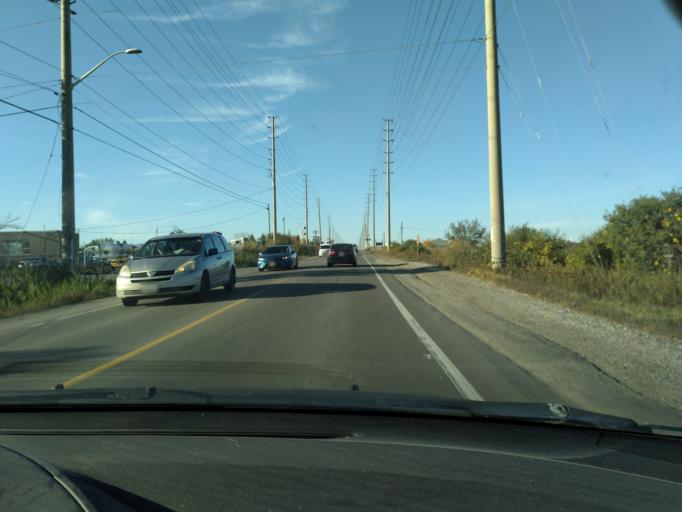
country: CA
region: Ontario
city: Brampton
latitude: 43.8633
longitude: -79.7043
